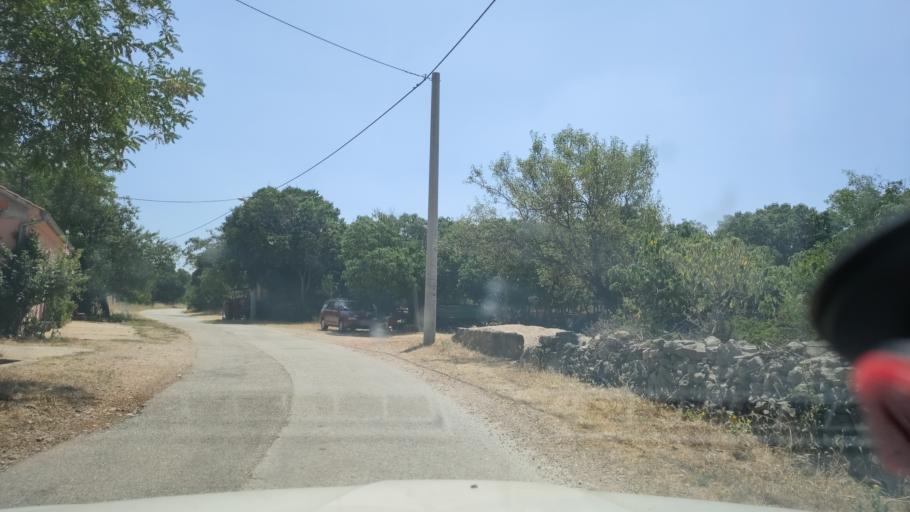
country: HR
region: Sibensko-Kniniska
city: Kistanje
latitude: 43.9570
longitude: 15.8772
